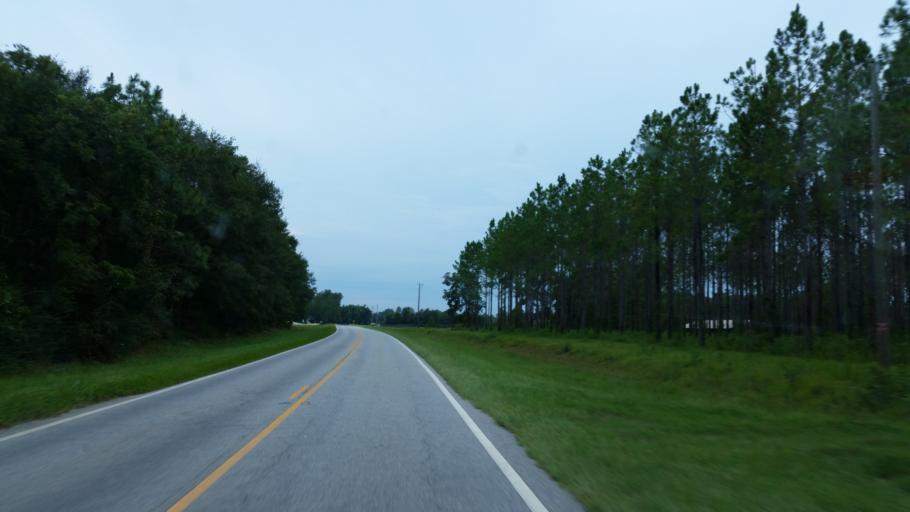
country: US
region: Georgia
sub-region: Lowndes County
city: Valdosta
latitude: 30.7456
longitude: -83.3112
